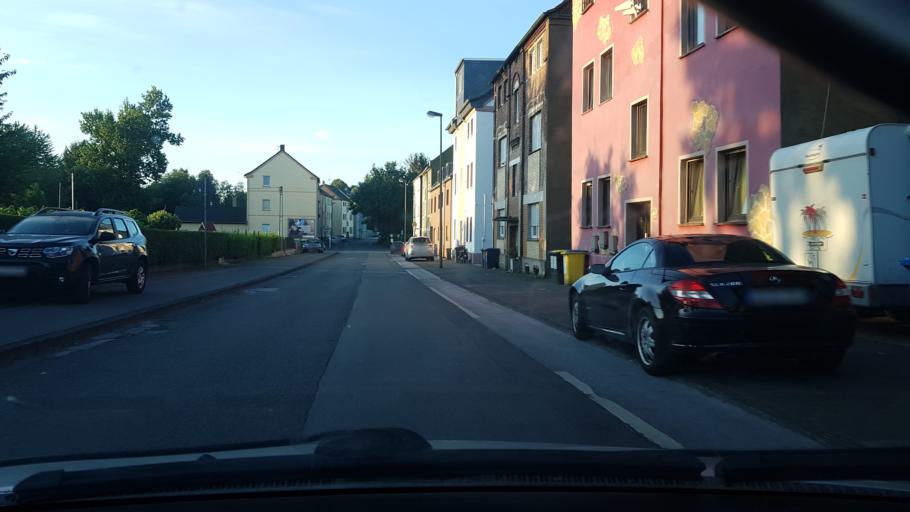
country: DE
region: North Rhine-Westphalia
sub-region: Regierungsbezirk Arnsberg
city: Dortmund
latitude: 51.5597
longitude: 7.4430
